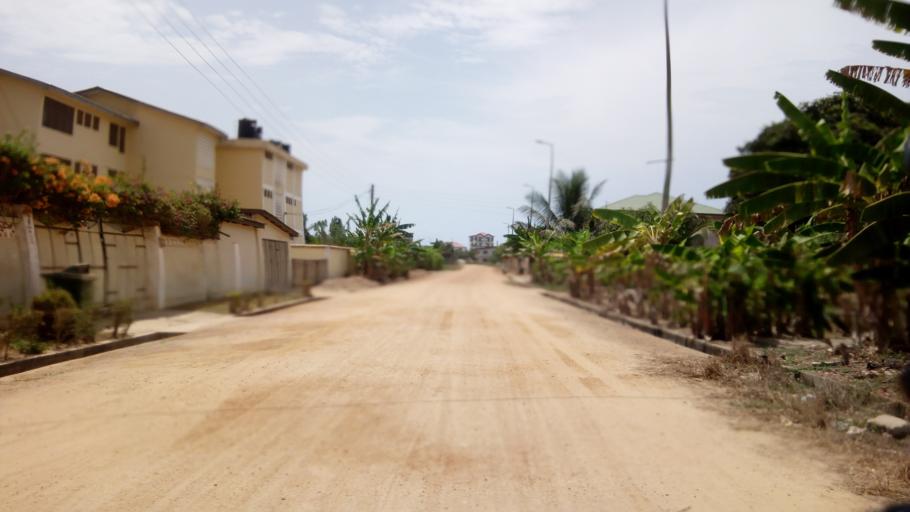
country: GH
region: Central
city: Cape Coast
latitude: 5.1284
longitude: -1.2805
